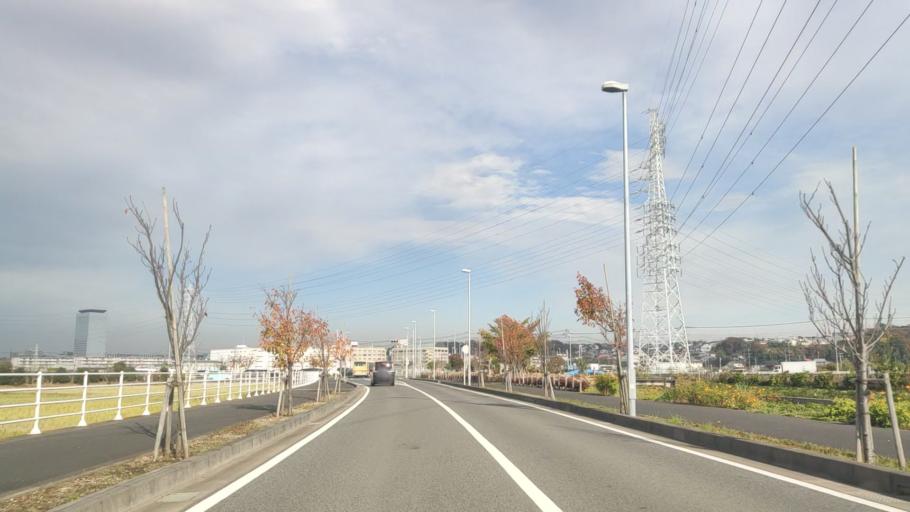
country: JP
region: Kanagawa
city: Atsugi
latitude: 35.4381
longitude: 139.3883
